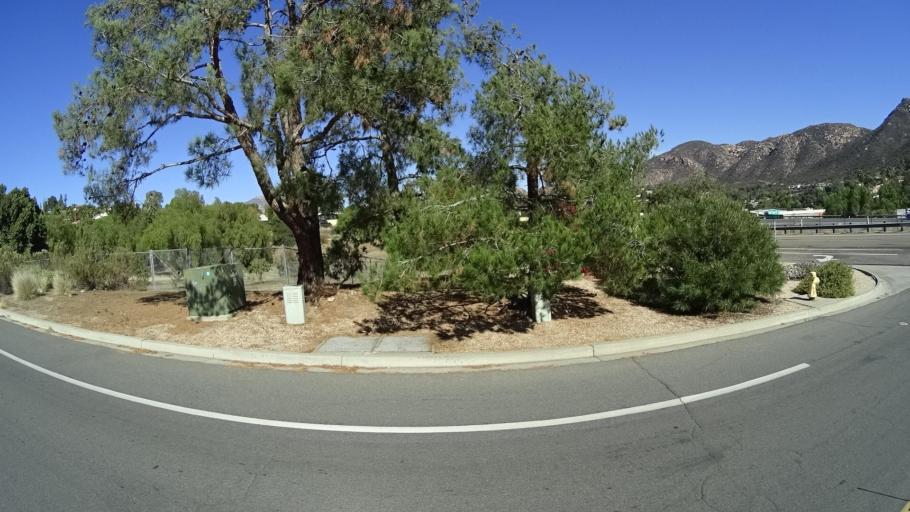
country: US
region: California
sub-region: San Diego County
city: Crest
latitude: 32.8486
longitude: -116.8739
